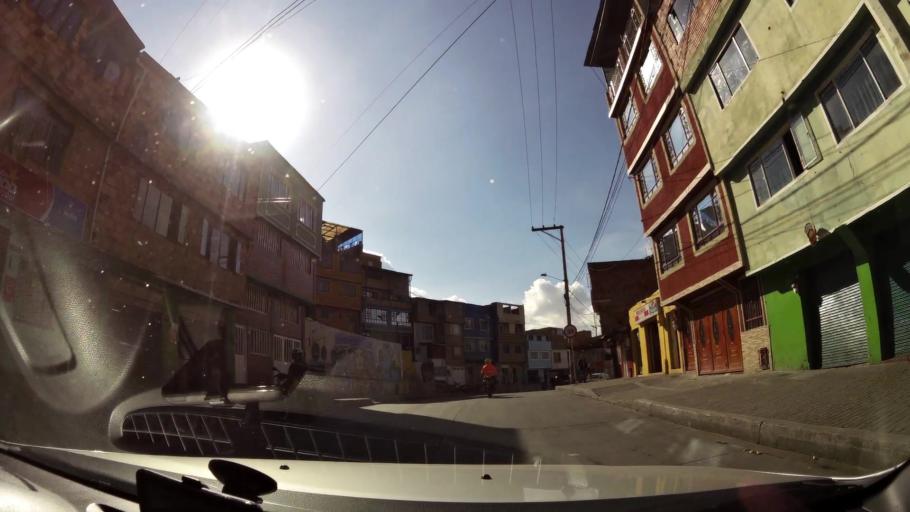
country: CO
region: Cundinamarca
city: Soacha
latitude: 4.5564
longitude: -74.1460
